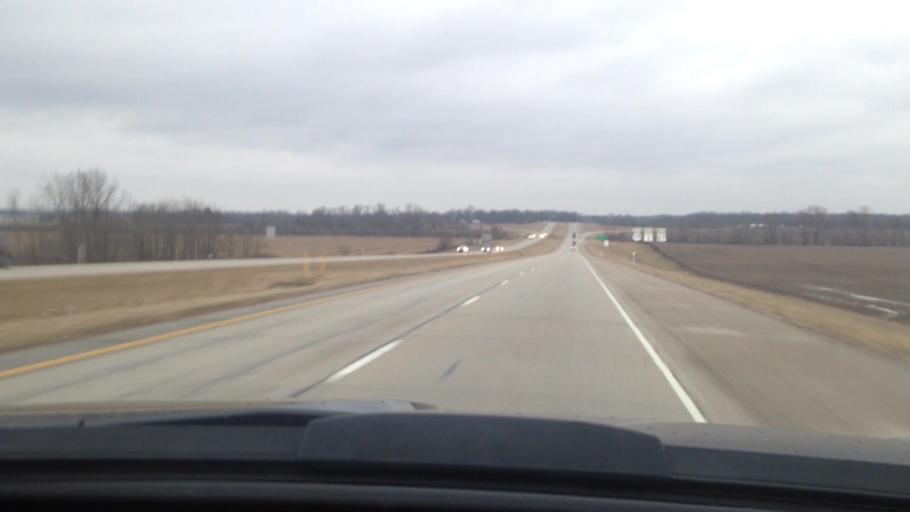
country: US
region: Indiana
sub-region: Delaware County
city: Muncie
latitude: 40.1894
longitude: -85.3365
